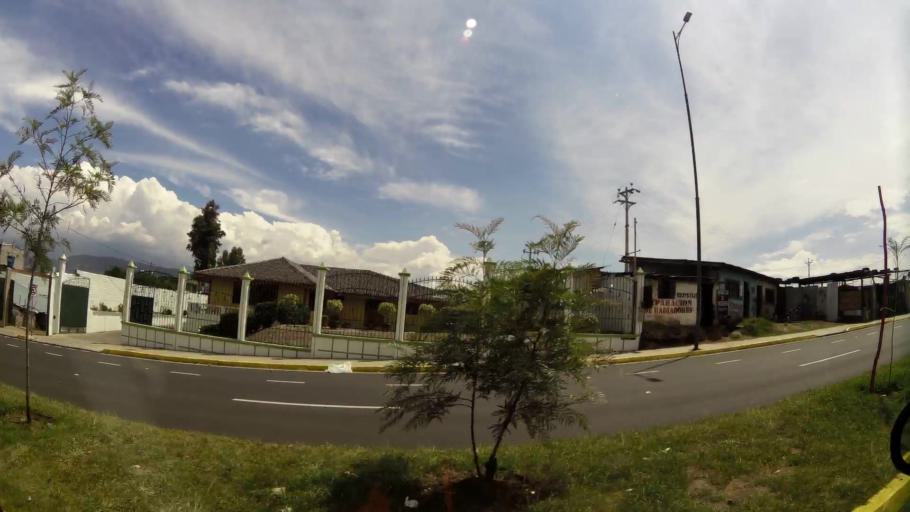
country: EC
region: Pichincha
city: Quito
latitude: -0.2051
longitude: -78.3786
